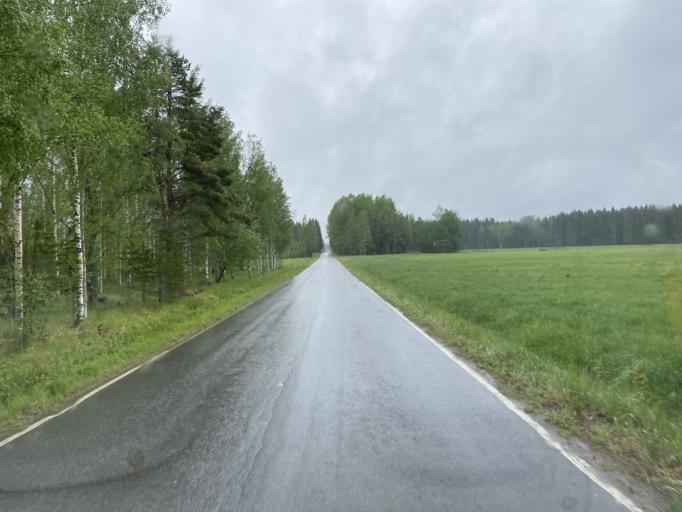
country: FI
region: Haeme
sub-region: Forssa
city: Humppila
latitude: 61.0638
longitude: 23.3240
